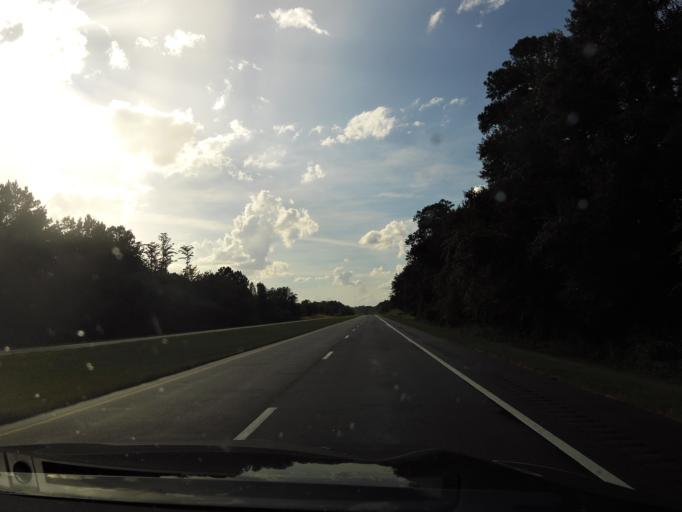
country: US
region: Georgia
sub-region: Brooks County
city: Quitman
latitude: 30.7867
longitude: -83.6298
